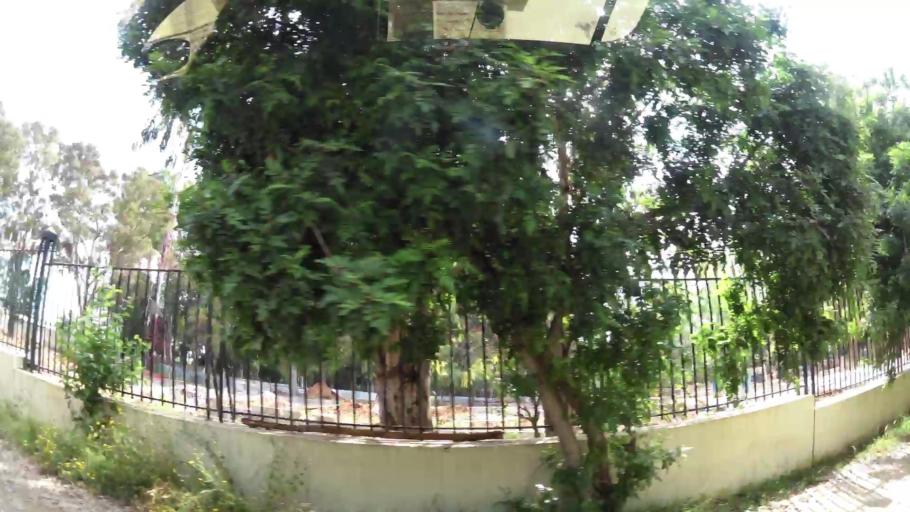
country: MA
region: Rabat-Sale-Zemmour-Zaer
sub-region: Rabat
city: Rabat
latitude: 33.9848
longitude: -6.8402
